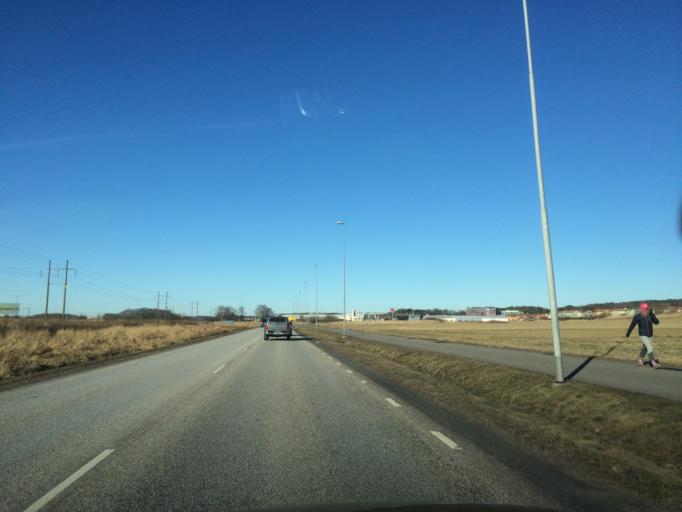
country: SE
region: Vaestra Goetaland
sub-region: Molndal
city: Moelndal
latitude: 57.6461
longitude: 11.9787
